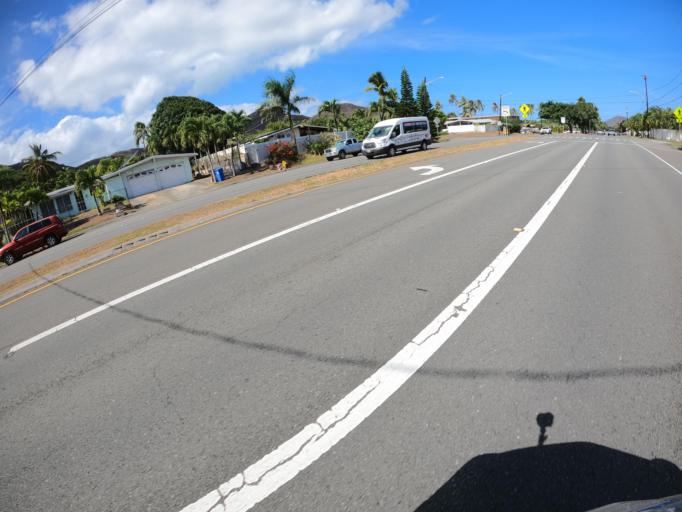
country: US
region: Hawaii
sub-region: Honolulu County
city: Kailua
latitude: 21.4156
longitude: -157.7510
